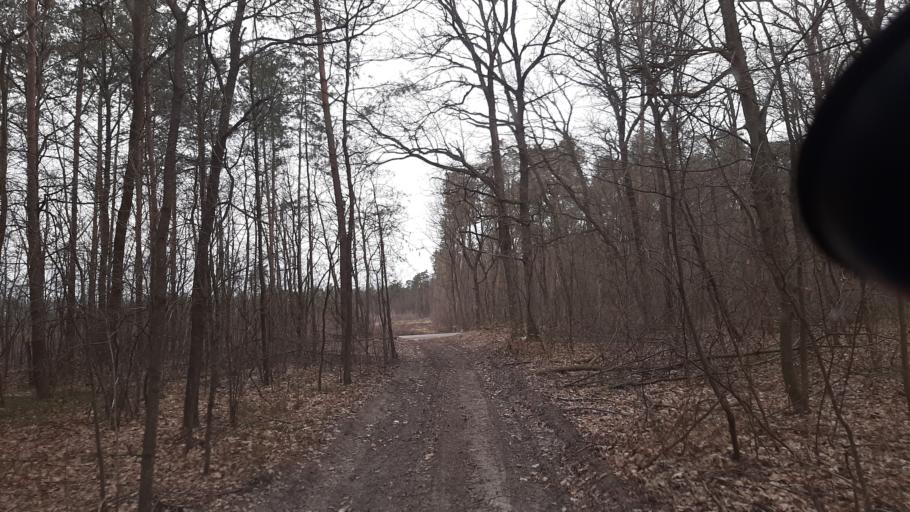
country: PL
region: Lublin Voivodeship
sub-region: Powiat lubelski
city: Garbow
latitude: 51.4056
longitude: 22.3650
